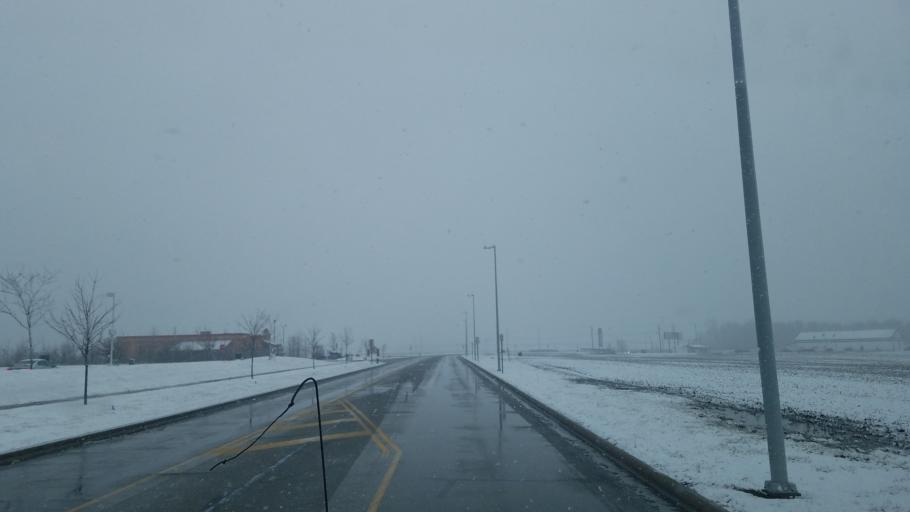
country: US
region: Ohio
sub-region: Union County
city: Marysville
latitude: 40.2276
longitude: -83.3392
